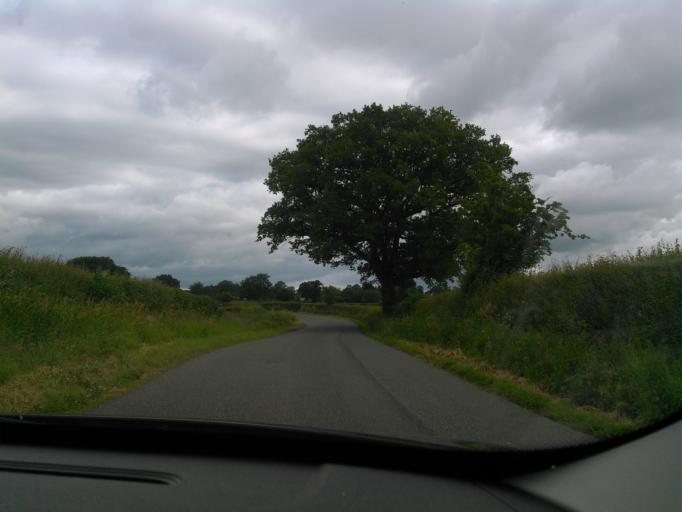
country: GB
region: England
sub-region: Shropshire
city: Wem
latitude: 52.8729
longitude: -2.7455
